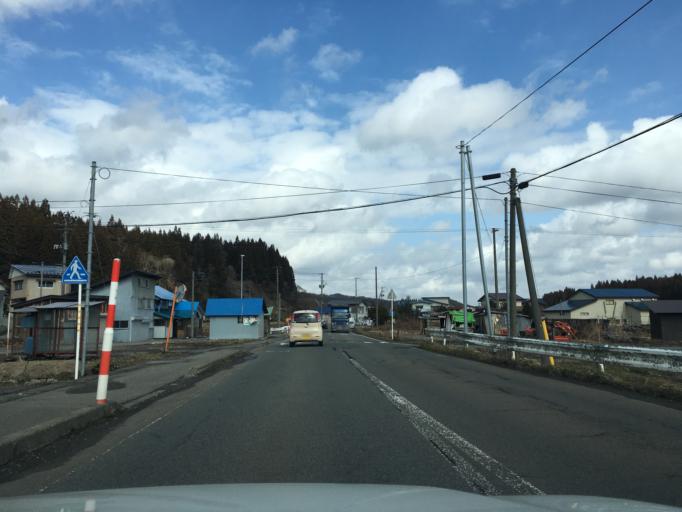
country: JP
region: Akita
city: Takanosu
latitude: 40.0331
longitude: 140.2750
